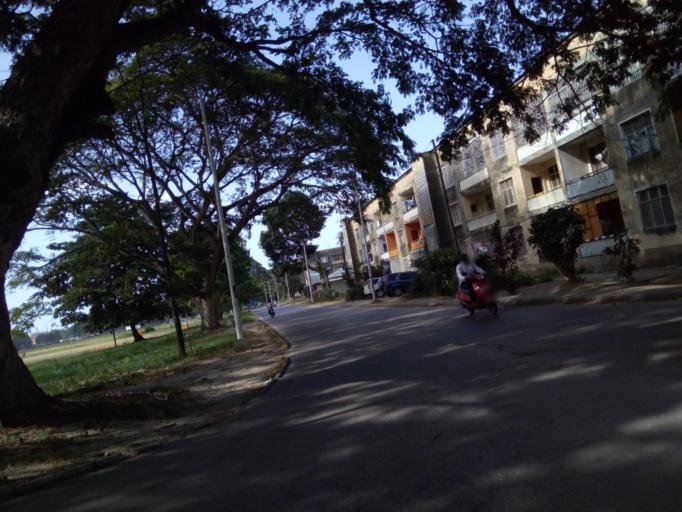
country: TZ
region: Zanzibar Urban/West
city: Zanzibar
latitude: -6.1721
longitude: 39.1946
